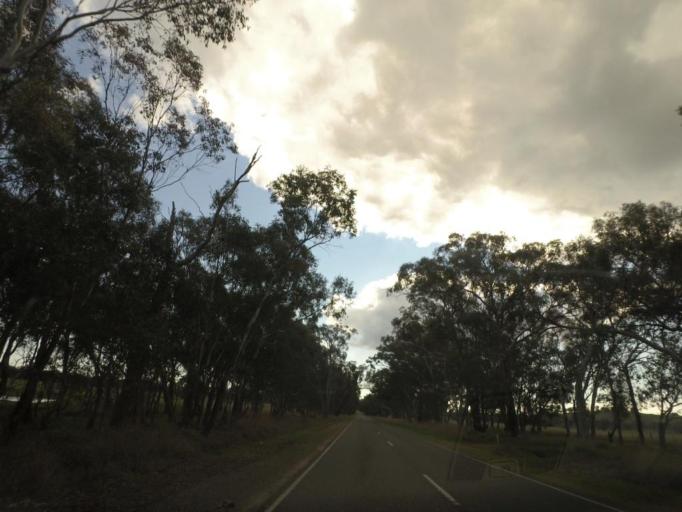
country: AU
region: New South Wales
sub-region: Corowa Shire
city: Howlong
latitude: -36.1919
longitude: 146.6149
